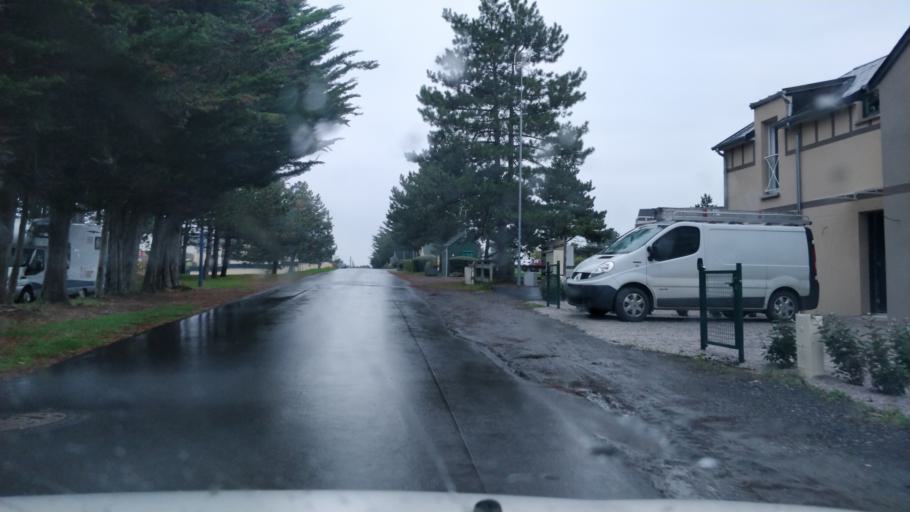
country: FR
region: Lower Normandy
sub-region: Departement de la Manche
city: Brehal
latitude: 48.8982
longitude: -1.5656
